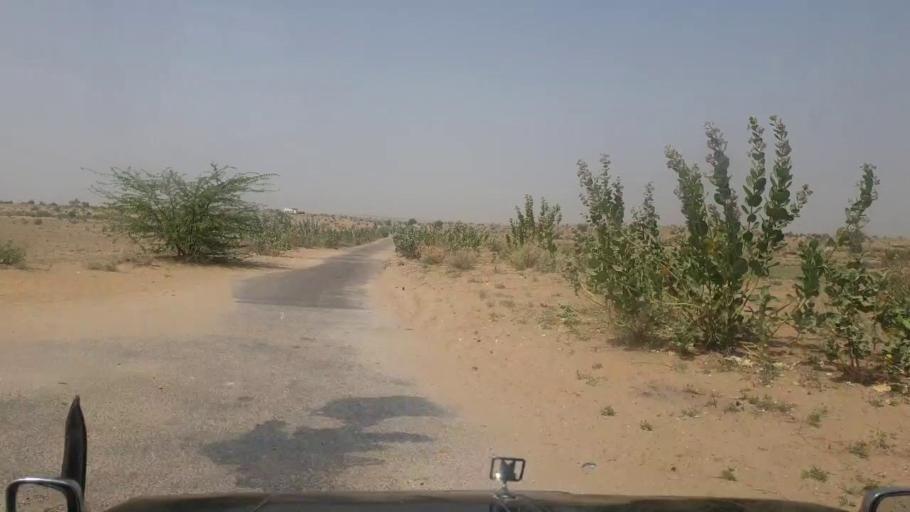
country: PK
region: Sindh
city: Islamkot
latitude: 25.1163
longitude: 70.2394
